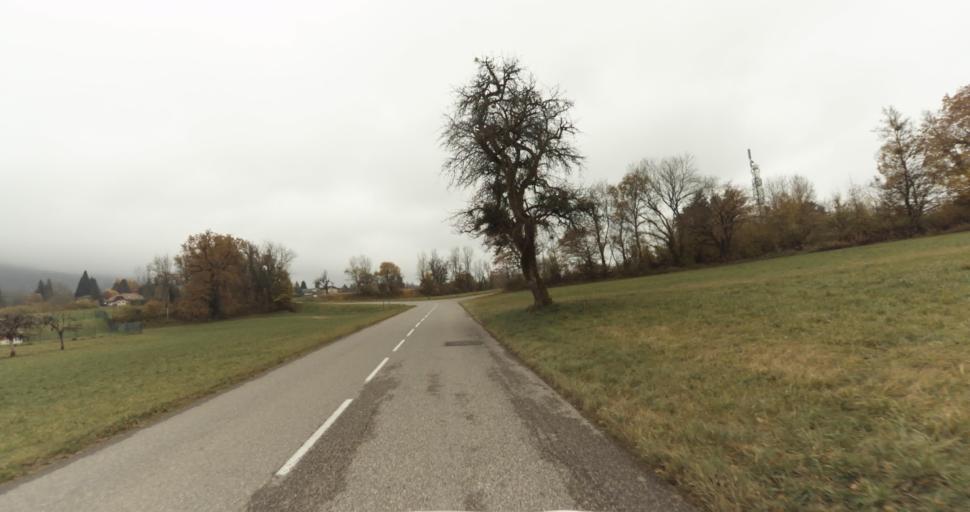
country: FR
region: Rhone-Alpes
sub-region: Departement de la Haute-Savoie
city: Seynod
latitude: 45.8527
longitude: 6.0846
